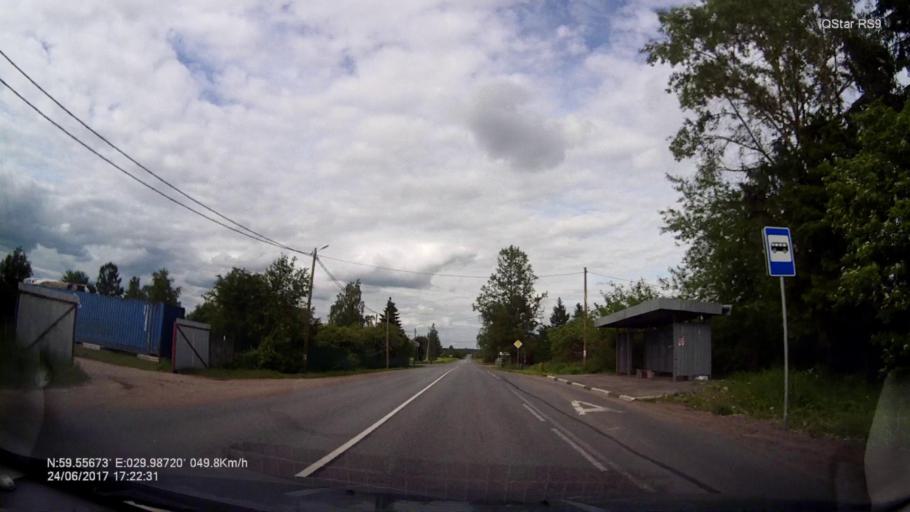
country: RU
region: Leningrad
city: Voyskovitsy
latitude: 59.5569
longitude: 29.9879
